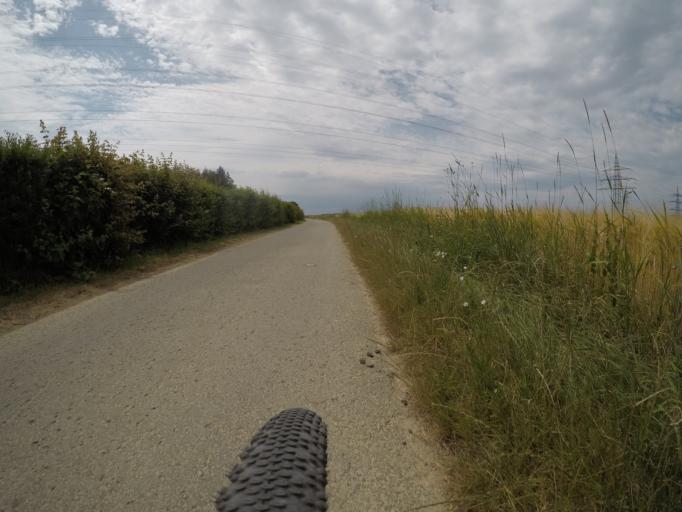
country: DE
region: Baden-Wuerttemberg
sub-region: Regierungsbezirk Stuttgart
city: Magstadt
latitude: 48.7152
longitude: 8.9529
